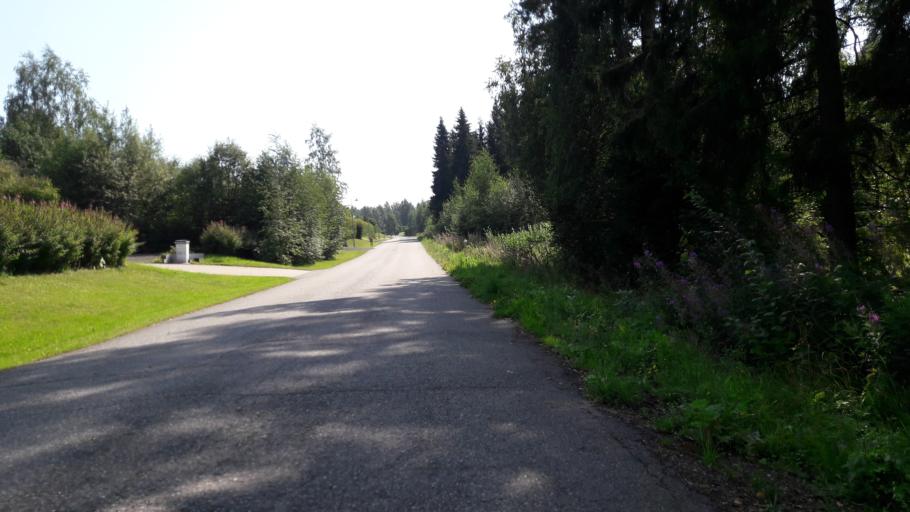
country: FI
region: North Karelia
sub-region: Joensuu
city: Joensuu
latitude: 62.5259
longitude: 29.8401
